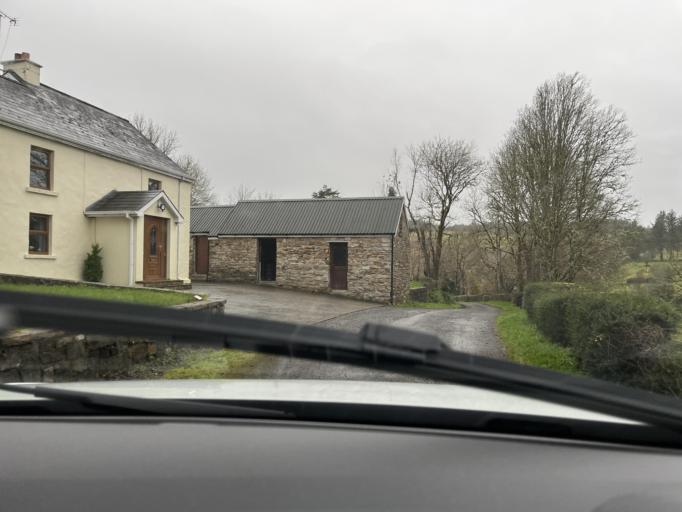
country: IE
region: Connaught
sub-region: County Leitrim
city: Manorhamilton
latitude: 54.2818
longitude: -8.0970
